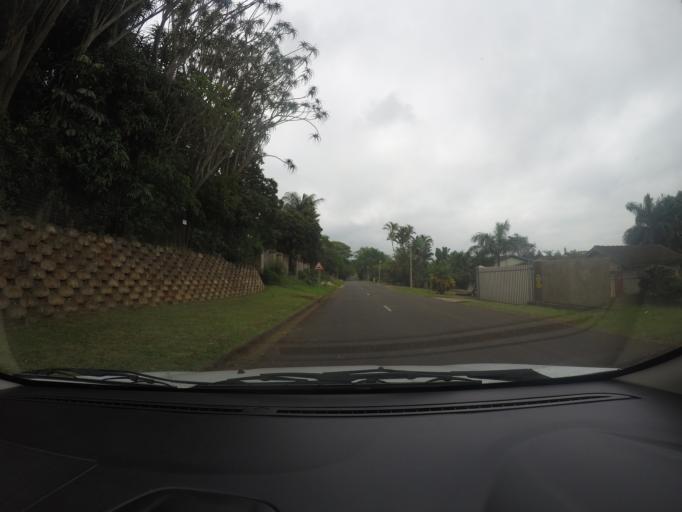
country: ZA
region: KwaZulu-Natal
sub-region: uThungulu District Municipality
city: Empangeni
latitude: -28.7555
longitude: 31.8898
